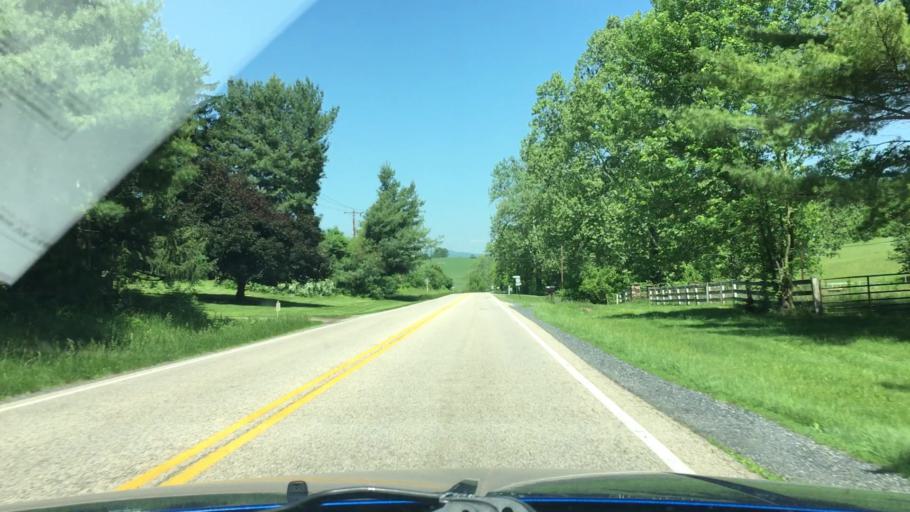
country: US
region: Virginia
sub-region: City of Staunton
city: Staunton
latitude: 38.1898
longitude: -79.1071
